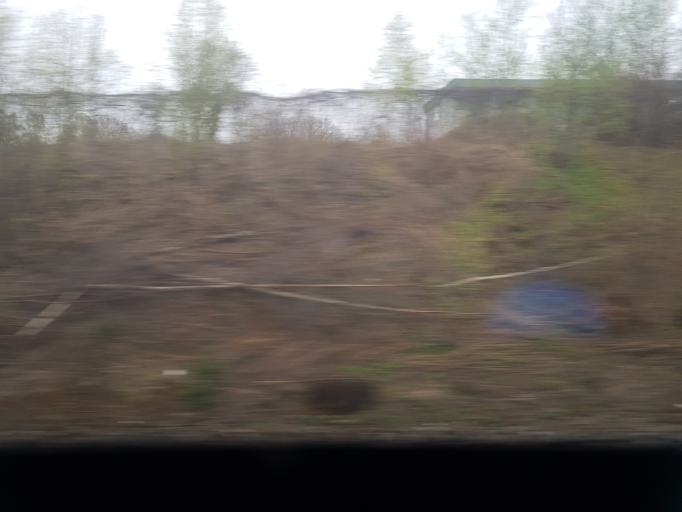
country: NO
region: Buskerud
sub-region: Lier
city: Lierbyen
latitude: 59.7549
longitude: 10.2680
